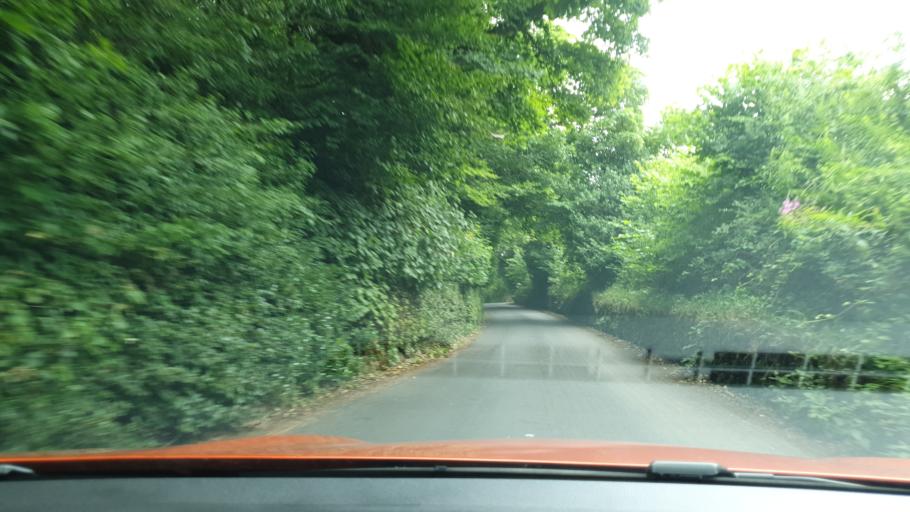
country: GB
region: England
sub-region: Cumbria
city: Penrith
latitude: 54.5892
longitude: -2.8430
